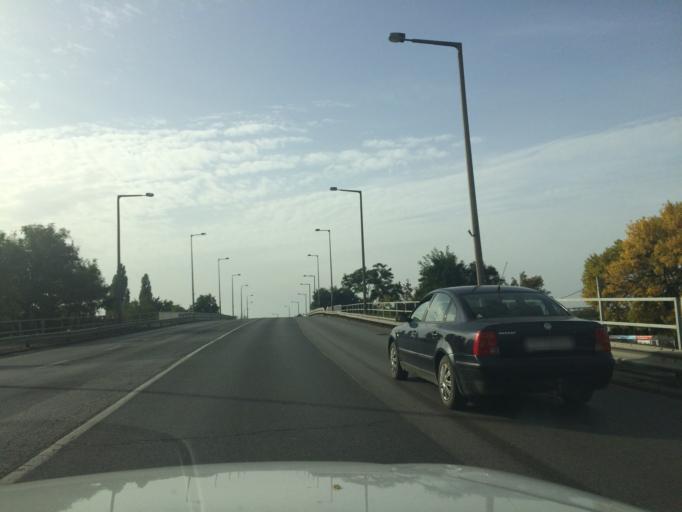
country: HU
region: Szabolcs-Szatmar-Bereg
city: Nyiregyhaza
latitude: 47.9418
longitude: 21.7198
